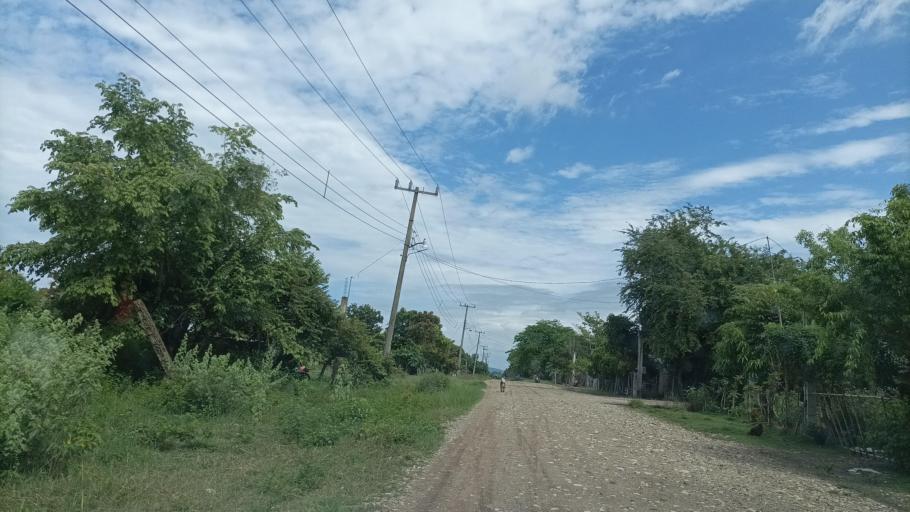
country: MX
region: Veracruz
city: Panuco
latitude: 21.9503
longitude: -98.1388
